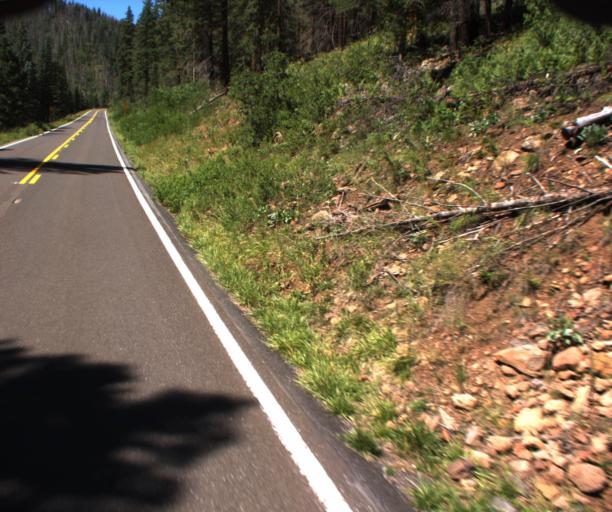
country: US
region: Arizona
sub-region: Apache County
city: Eagar
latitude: 33.6556
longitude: -109.2680
